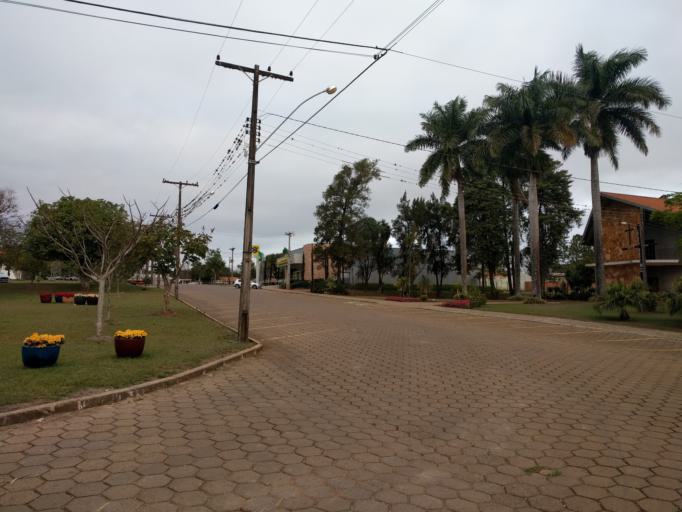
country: BR
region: Sao Paulo
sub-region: Paranapanema
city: Paranapanema
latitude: -23.4333
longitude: -48.8747
